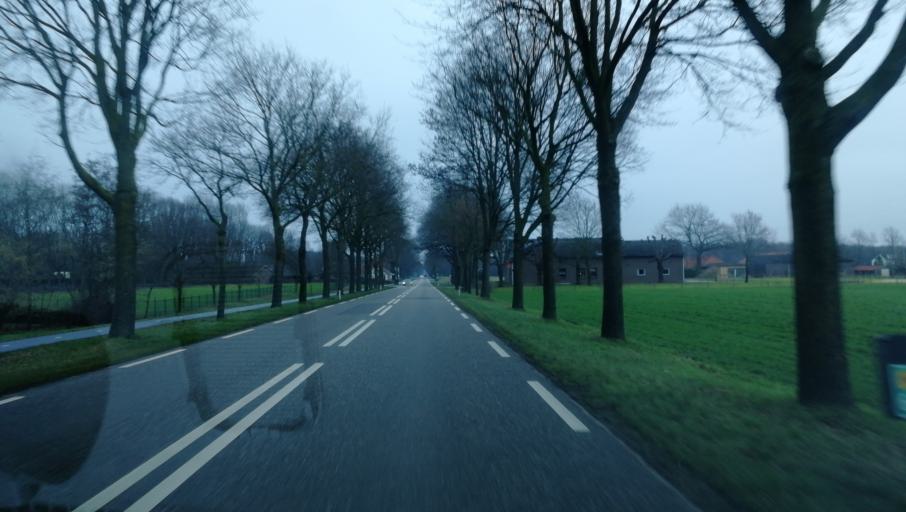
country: NL
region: Limburg
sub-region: Gemeente Beesel
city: Reuver
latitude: 51.3083
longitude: 6.0659
